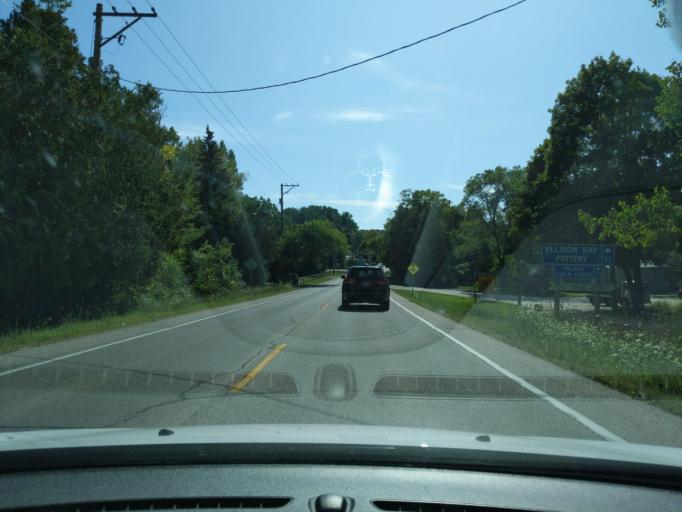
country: US
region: Michigan
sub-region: Delta County
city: Escanaba
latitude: 45.2565
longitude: -87.0699
